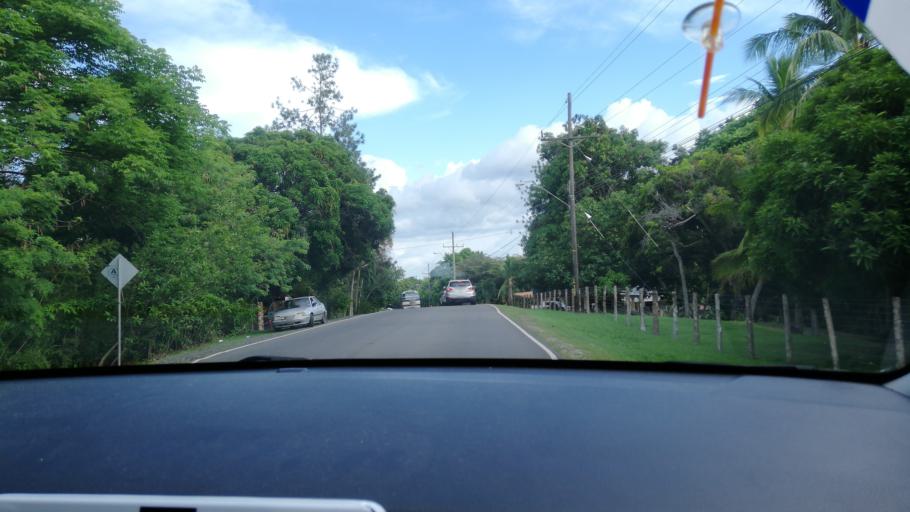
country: PA
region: Panama
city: Las Colinas
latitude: 8.5212
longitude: -80.0370
